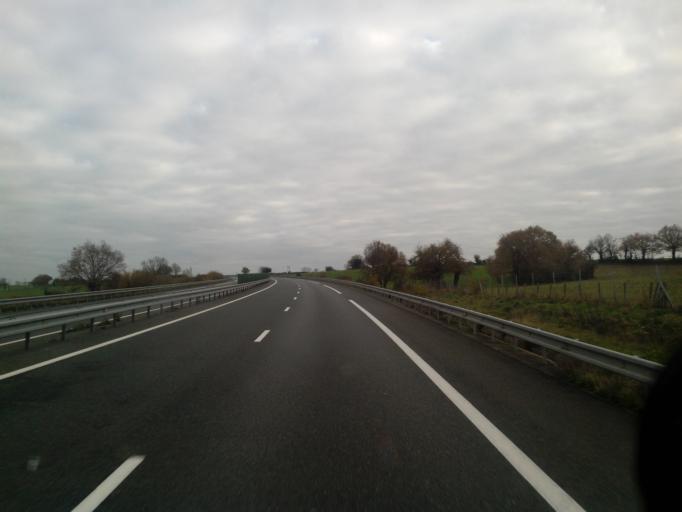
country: FR
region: Poitou-Charentes
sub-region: Departement des Deux-Sevres
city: Combrand
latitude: 46.9090
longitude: -0.6795
